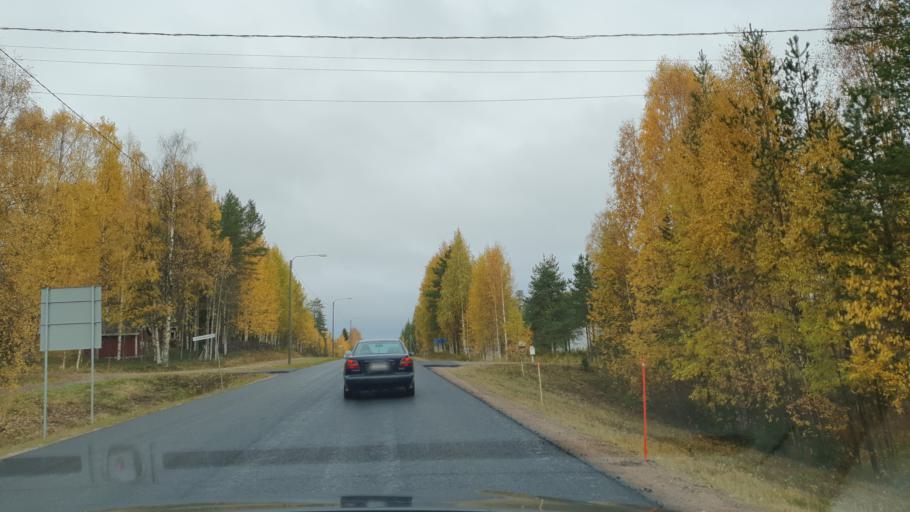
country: FI
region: Lapland
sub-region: Rovaniemi
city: Rovaniemi
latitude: 66.6513
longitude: 25.4527
